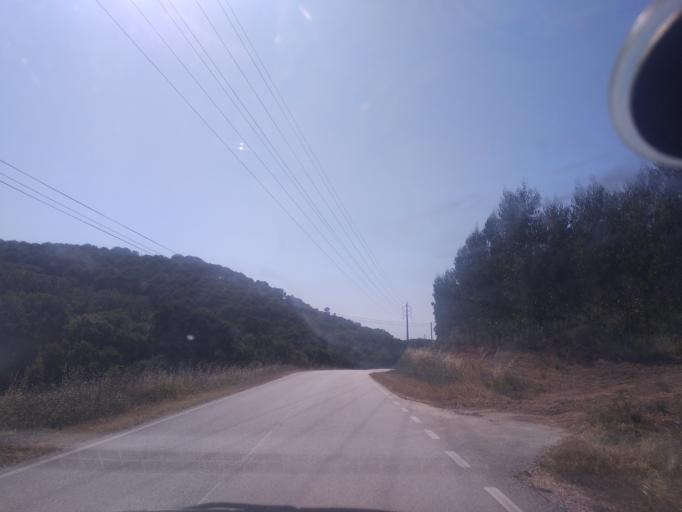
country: PT
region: Faro
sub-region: Aljezur
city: Aljezur
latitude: 37.2163
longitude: -8.7877
